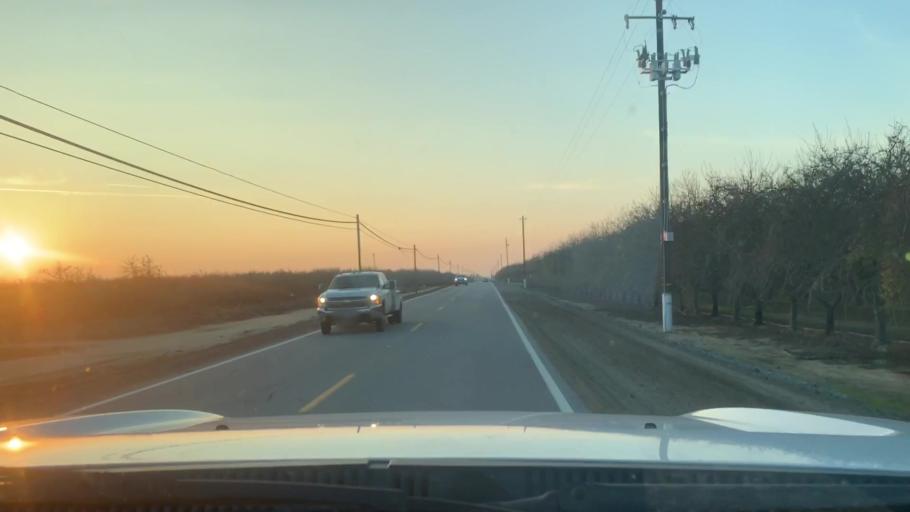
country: US
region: California
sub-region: Kern County
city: Rosedale
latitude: 35.3835
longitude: -119.2231
